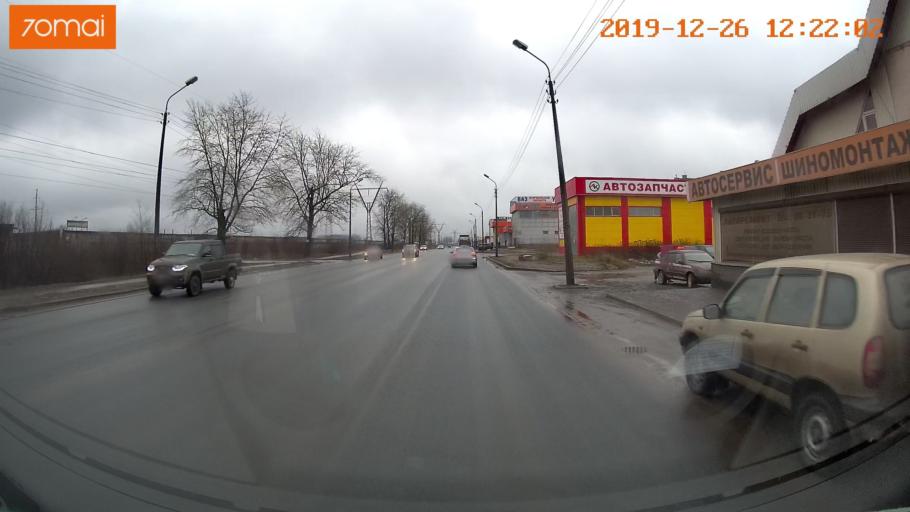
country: RU
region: Vologda
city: Cherepovets
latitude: 59.1511
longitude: 37.9399
